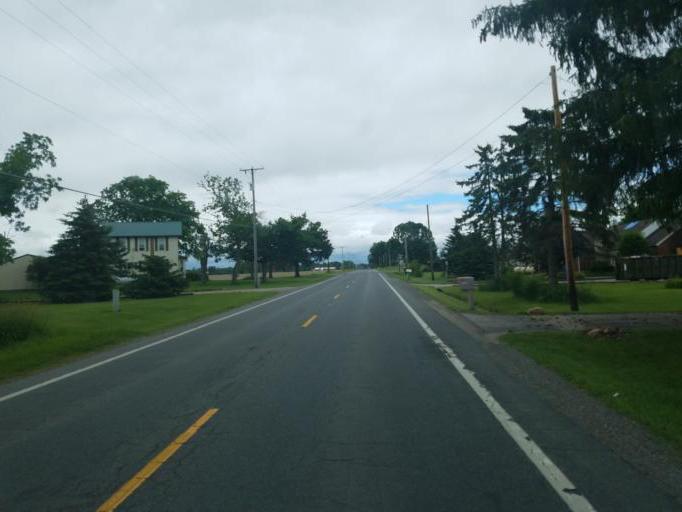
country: US
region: Ohio
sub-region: Crawford County
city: Galion
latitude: 40.7437
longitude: -82.8402
